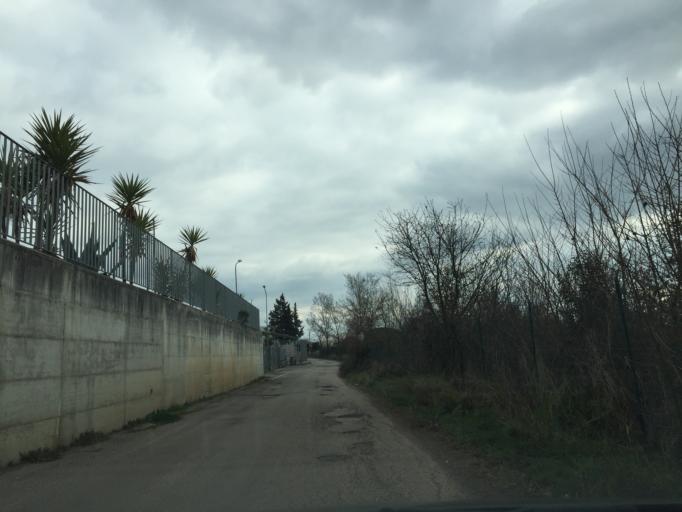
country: IT
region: Latium
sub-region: Provincia di Frosinone
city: Cassino
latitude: 41.4820
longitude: 13.8047
